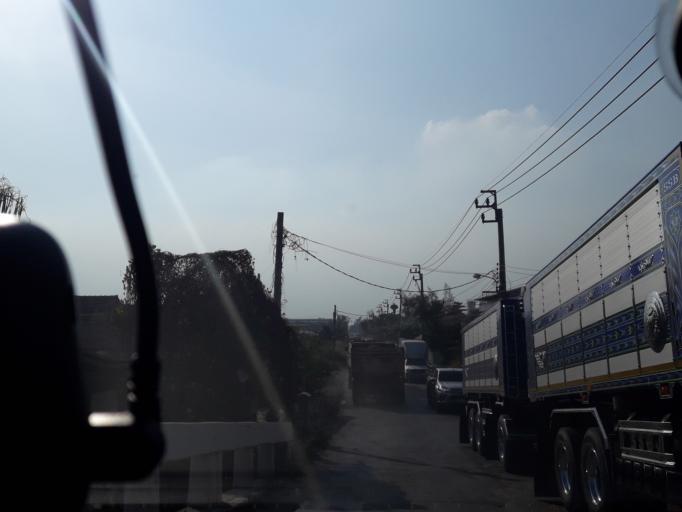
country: TH
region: Pathum Thani
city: Lam Luk Ka
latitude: 13.9118
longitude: 100.7286
